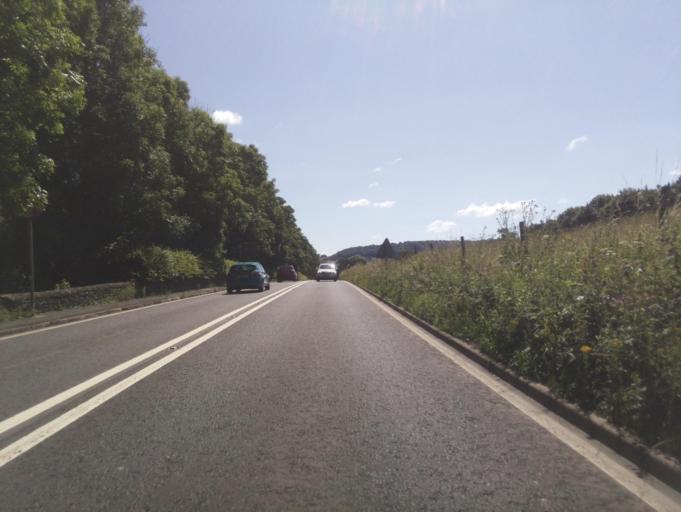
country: GB
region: England
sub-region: Derbyshire
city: Bakewell
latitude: 53.1946
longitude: -1.6566
